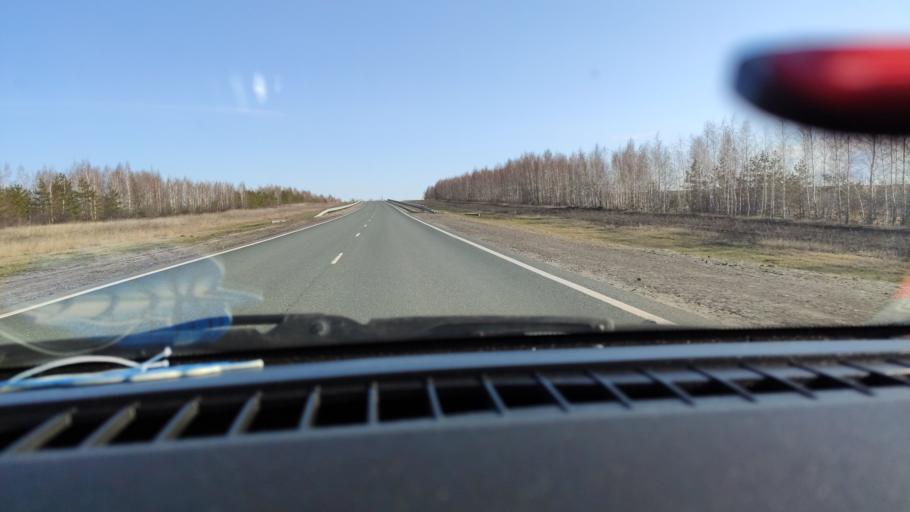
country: RU
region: Saratov
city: Dukhovnitskoye
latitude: 52.8307
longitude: 48.2390
